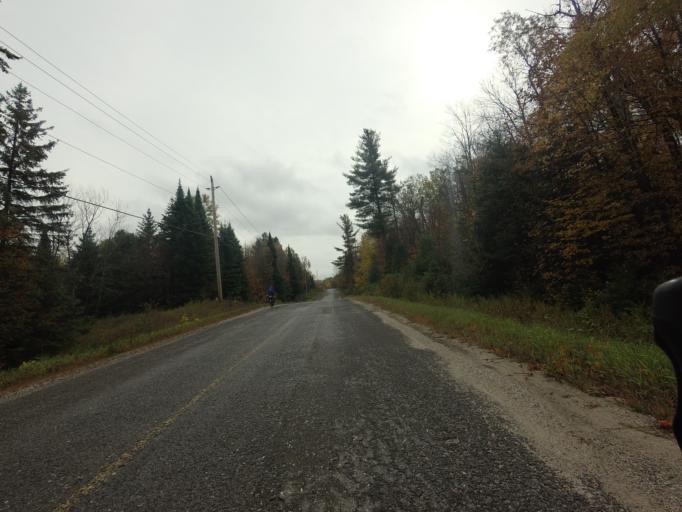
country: CA
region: Ontario
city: Perth
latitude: 45.1172
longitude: -76.5146
